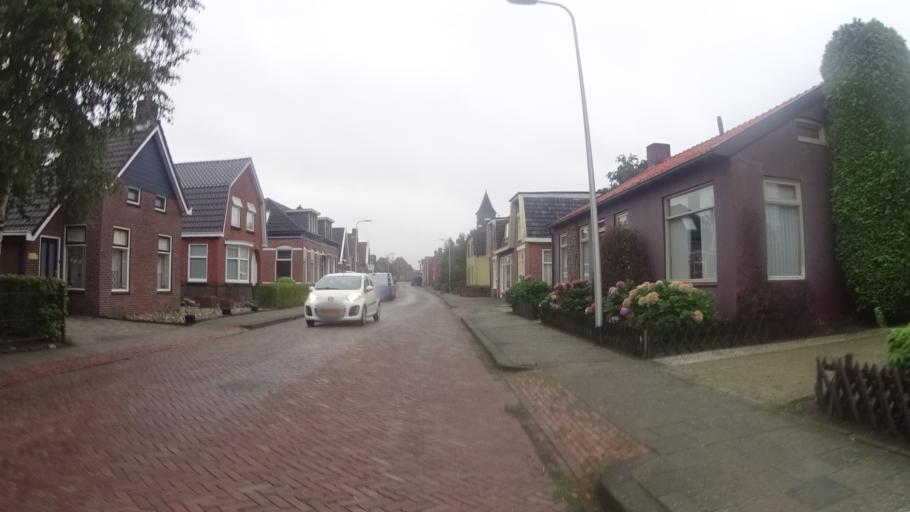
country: NL
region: Groningen
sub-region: Gemeente  Oldambt
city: Winschoten
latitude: 53.1790
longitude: 6.9682
